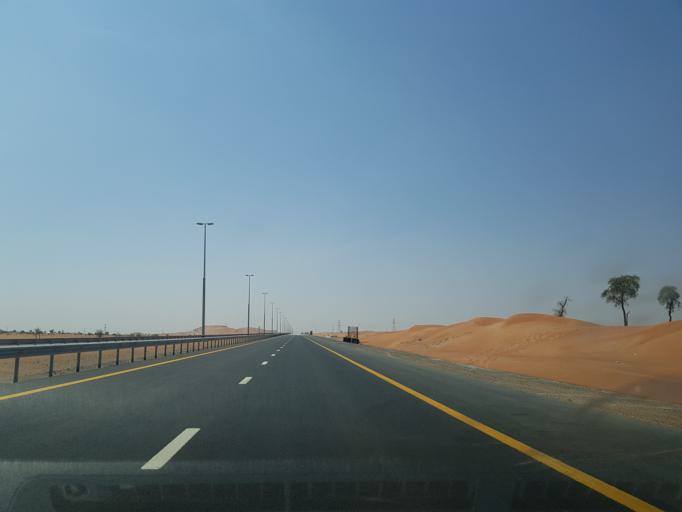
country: AE
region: Ash Shariqah
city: Adh Dhayd
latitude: 25.2432
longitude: 55.8672
